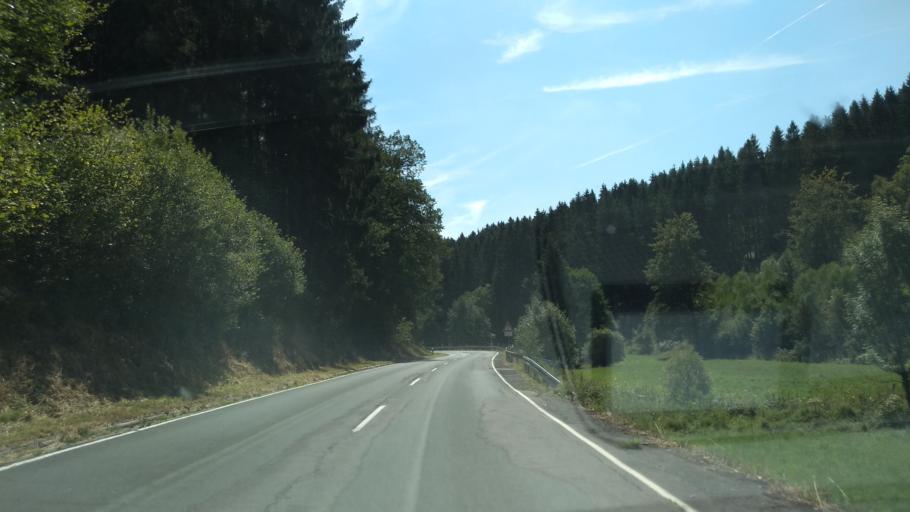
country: DE
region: North Rhine-Westphalia
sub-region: Regierungsbezirk Arnsberg
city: Drolshagen
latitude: 51.0898
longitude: 7.7884
